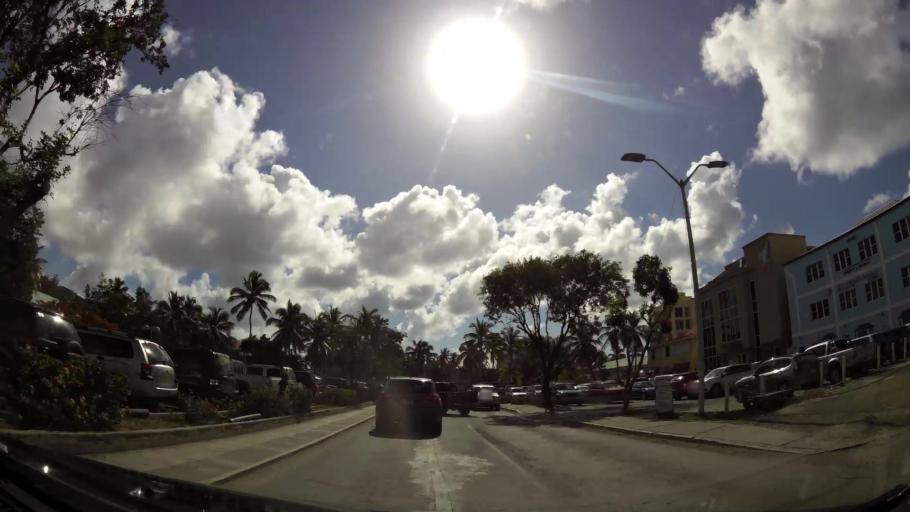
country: VG
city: Road Town
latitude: 18.4230
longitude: -64.6189
